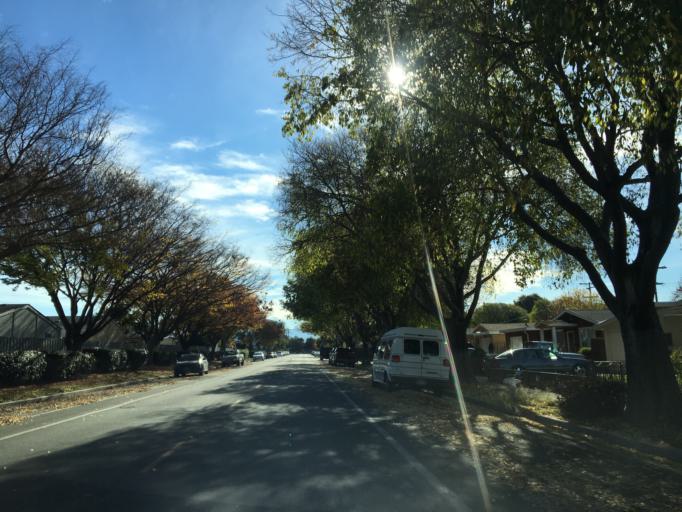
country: US
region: California
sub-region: Santa Clara County
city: Sunnyvale
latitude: 37.4008
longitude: -122.0216
